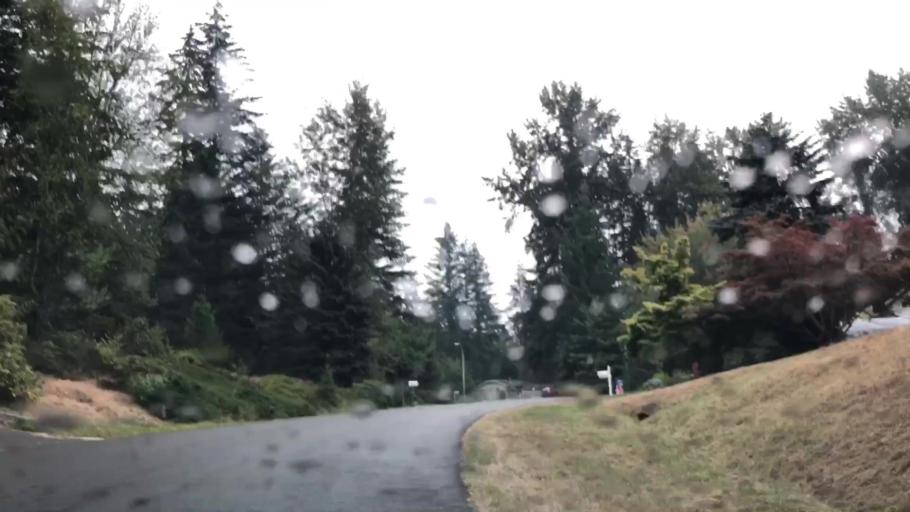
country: US
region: Washington
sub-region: King County
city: Cottage Lake
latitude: 47.7564
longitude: -122.0640
